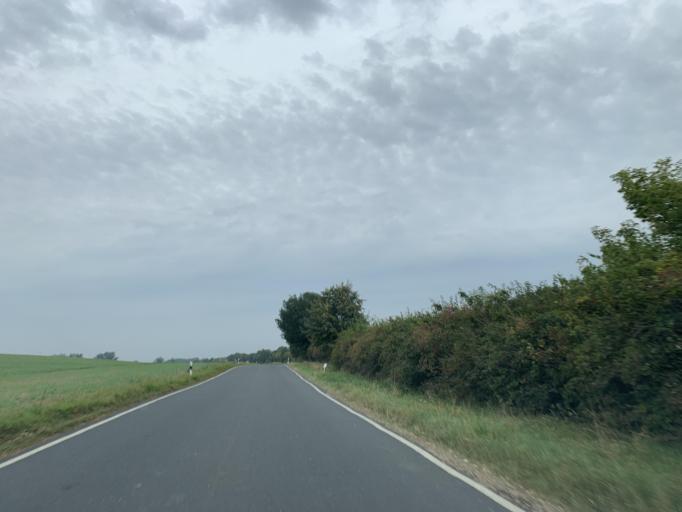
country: DE
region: Brandenburg
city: Mittenwalde
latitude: 53.3186
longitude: 13.6959
